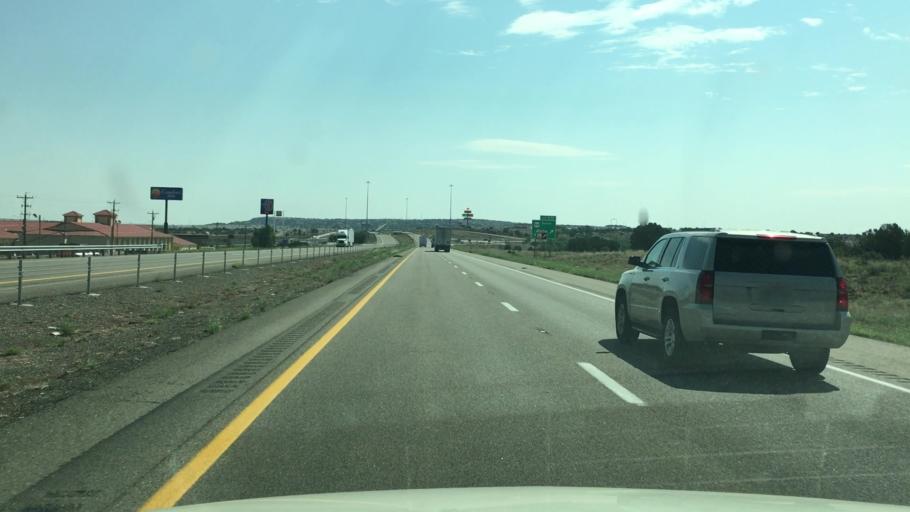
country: US
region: New Mexico
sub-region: Guadalupe County
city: Santa Rosa
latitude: 34.9460
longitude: -104.6499
